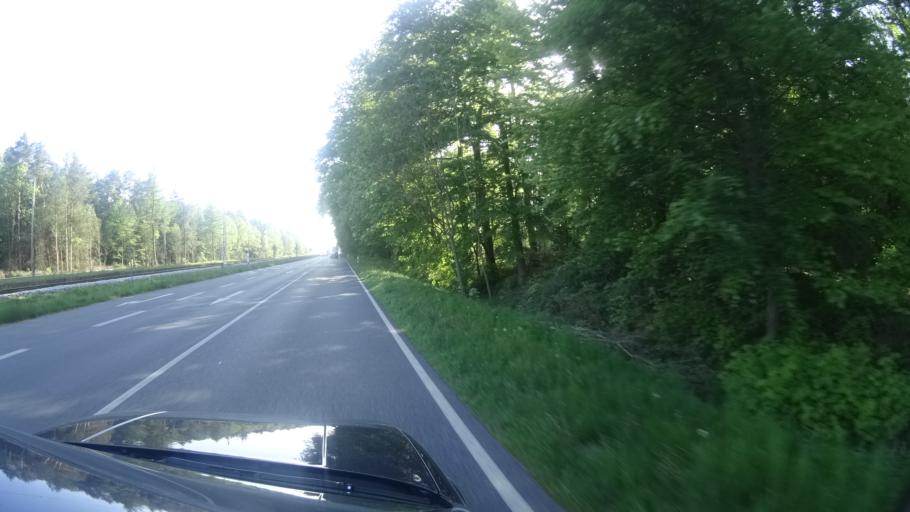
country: DE
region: Mecklenburg-Vorpommern
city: Gelbensande
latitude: 54.1870
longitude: 12.2742
